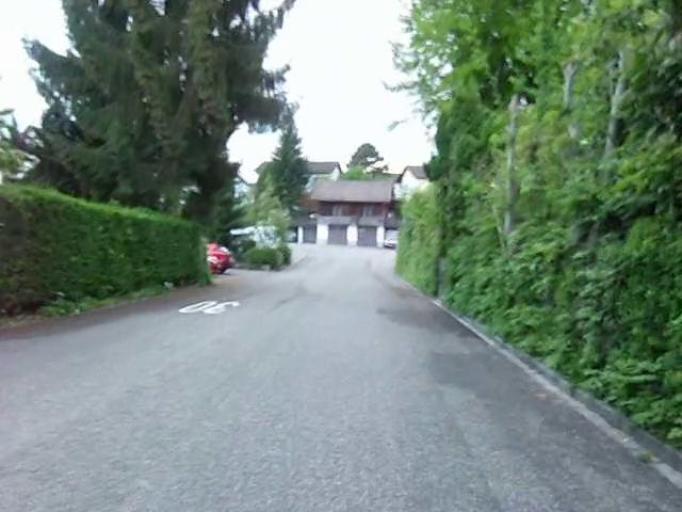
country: CH
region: Zurich
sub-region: Bezirk Hinwil
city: Rueti / Dorfzentrum, Suedl. Teil
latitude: 47.2539
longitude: 8.8569
